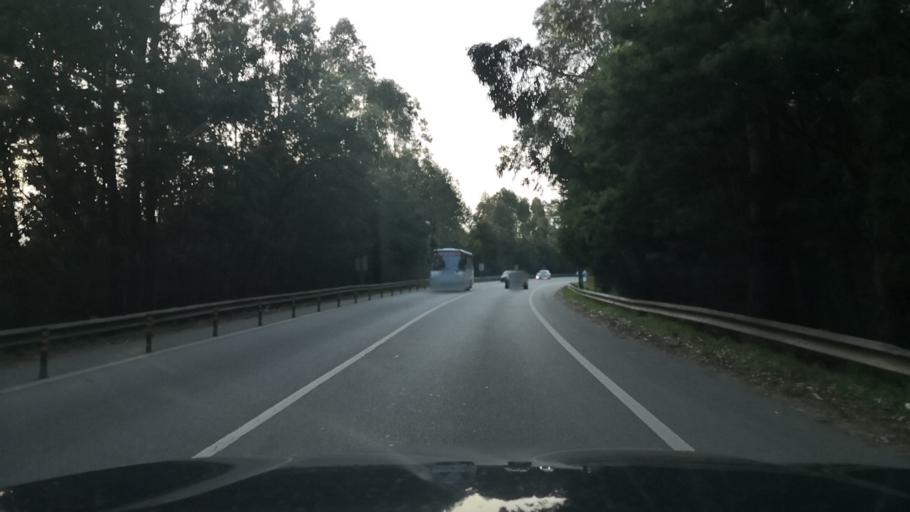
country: PT
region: Porto
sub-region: Valongo
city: Valongo
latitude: 41.1968
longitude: -8.5213
